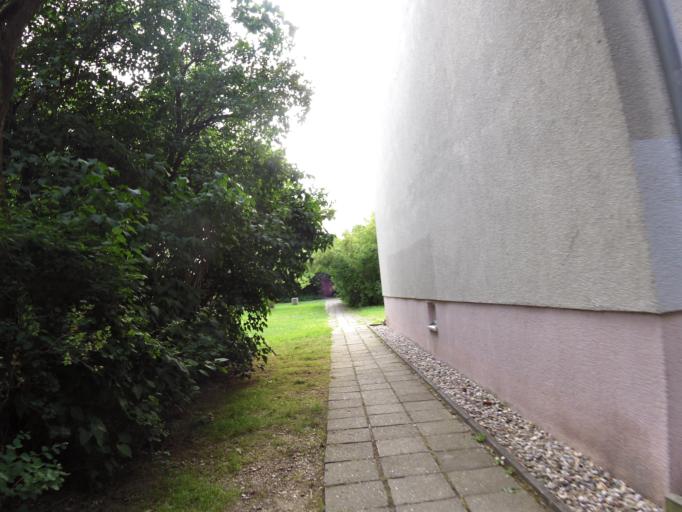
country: DE
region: Saxony
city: Markkleeberg
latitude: 51.3077
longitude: 12.3192
